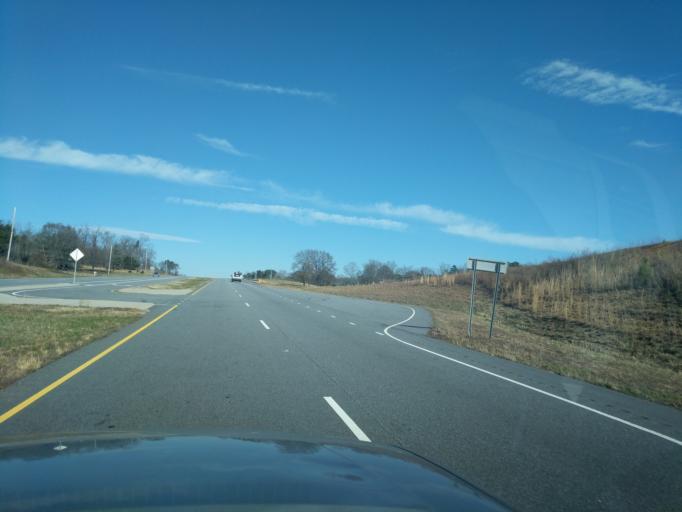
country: US
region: South Carolina
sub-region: Spartanburg County
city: Mayo
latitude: 35.1929
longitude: -81.8410
